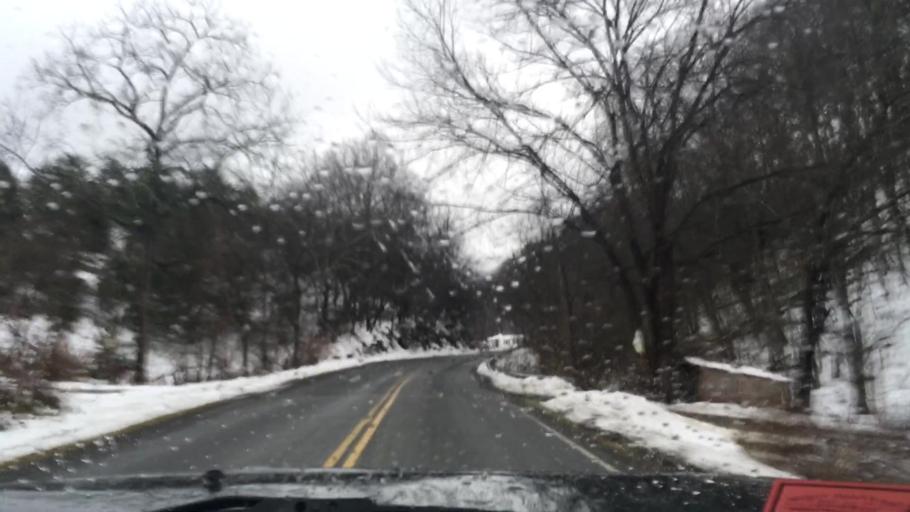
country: US
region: Virginia
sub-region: Pulaski County
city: Pulaski
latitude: 37.0129
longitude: -80.7012
